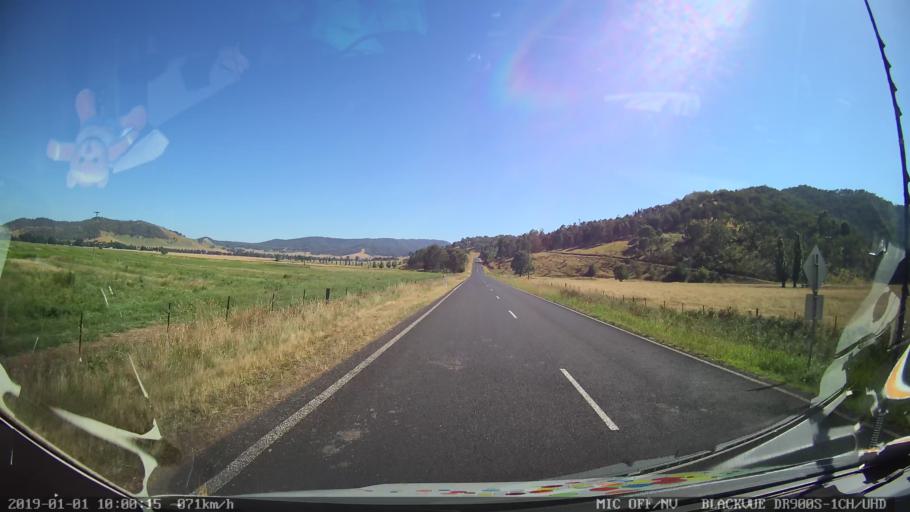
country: AU
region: New South Wales
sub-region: Snowy River
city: Jindabyne
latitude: -36.2042
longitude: 148.1020
